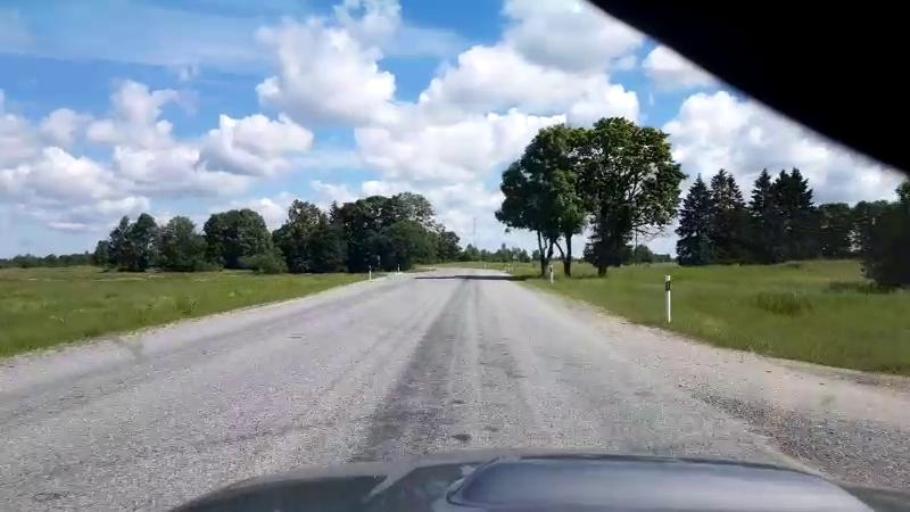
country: EE
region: Laeaene-Virumaa
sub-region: Tapa vald
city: Tapa
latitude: 59.2405
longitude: 25.9256
